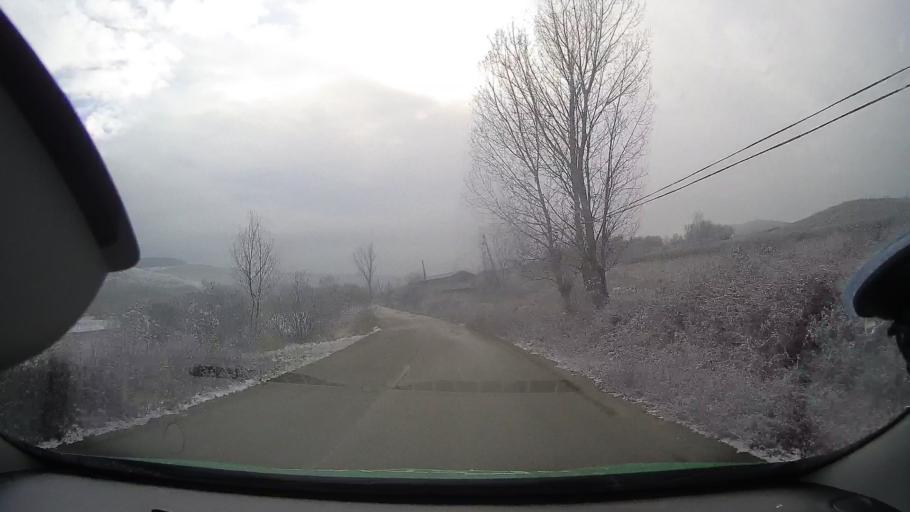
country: RO
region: Mures
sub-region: Comuna Chetani
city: Chetani
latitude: 46.4200
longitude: 24.0149
